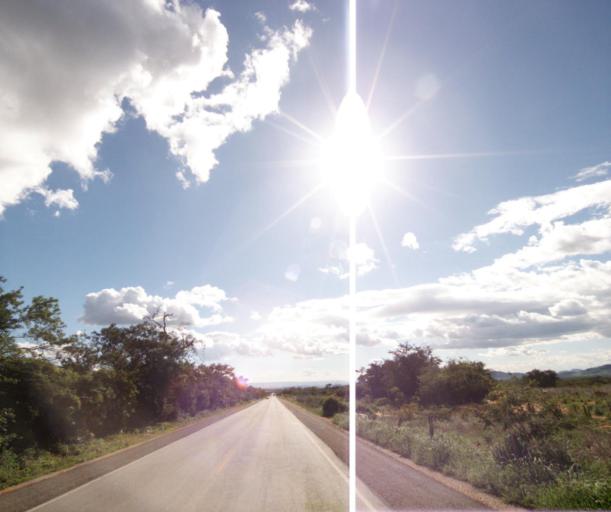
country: BR
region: Bahia
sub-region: Caetite
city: Caetite
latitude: -14.1257
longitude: -42.6192
